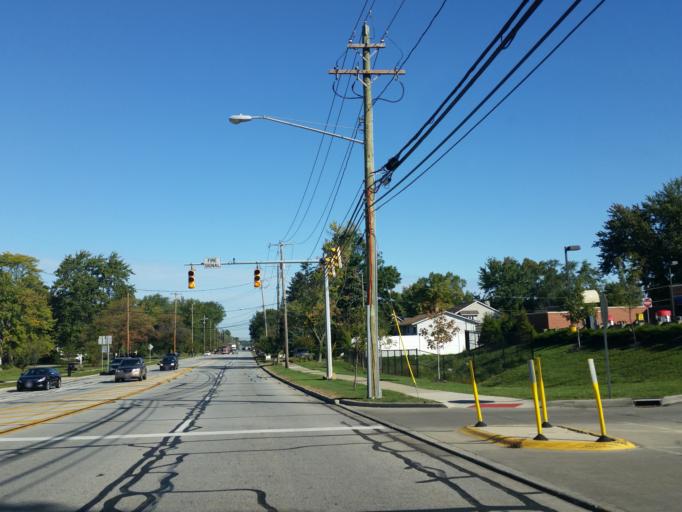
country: US
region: Ohio
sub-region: Cuyahoga County
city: Westlake
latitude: 41.4566
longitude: -81.9021
